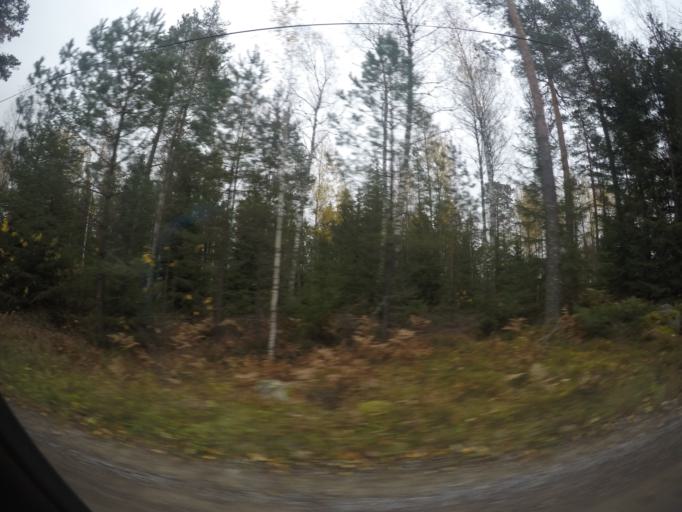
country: SE
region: Vaestmanland
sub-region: Kopings Kommun
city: Koping
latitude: 59.6044
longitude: 16.0778
